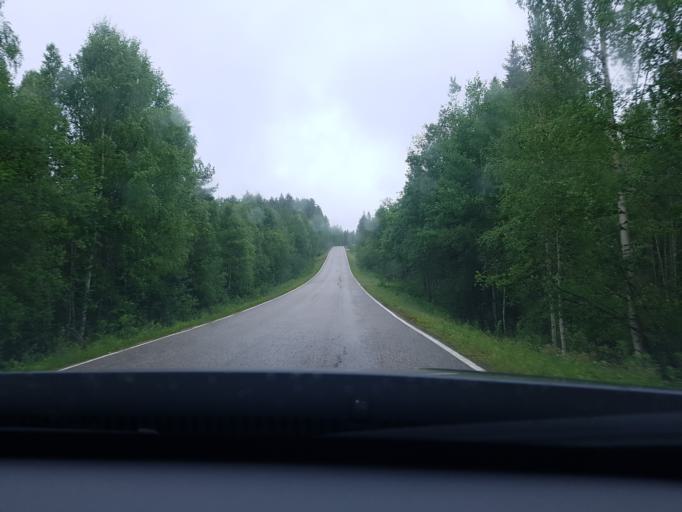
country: FI
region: Kainuu
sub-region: Kehys-Kainuu
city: Kuhmo
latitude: 64.3098
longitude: 29.4298
